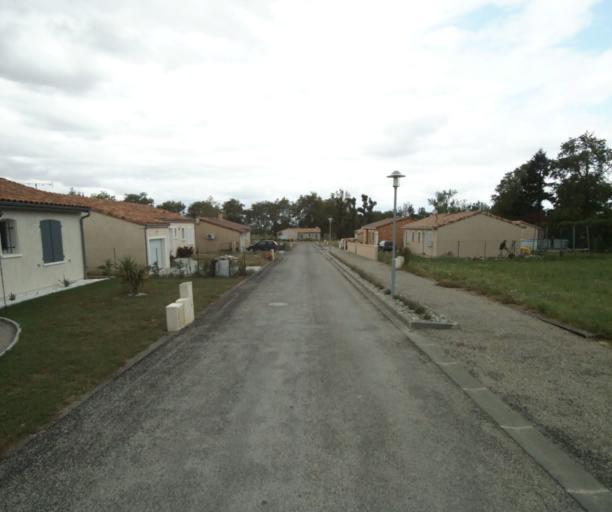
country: FR
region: Midi-Pyrenees
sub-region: Departement du Tarn
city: Soreze
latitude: 43.4550
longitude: 2.0657
